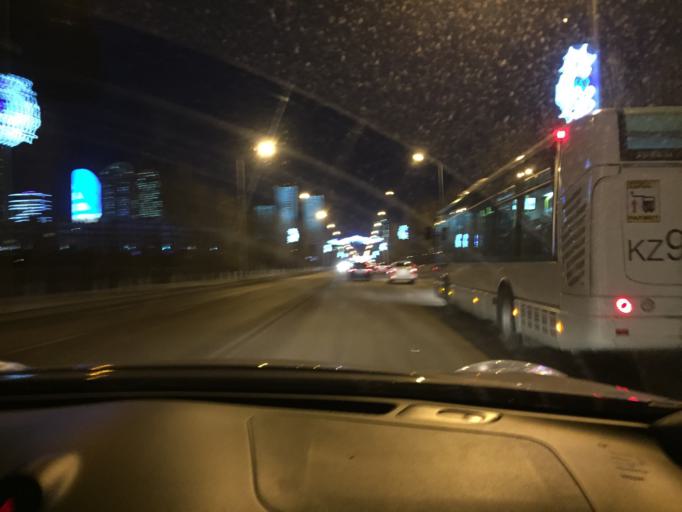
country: KZ
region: Astana Qalasy
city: Astana
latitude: 51.1294
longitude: 71.4073
